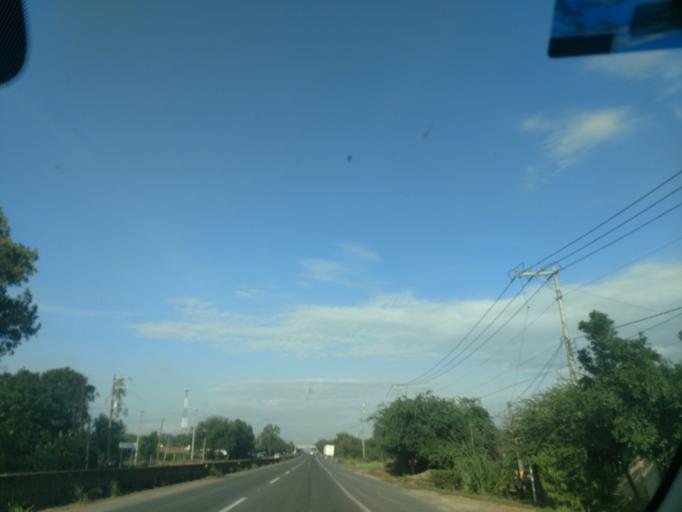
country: MX
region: Jalisco
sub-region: Ameca
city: Los Pocitos
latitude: 20.5375
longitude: -103.9320
